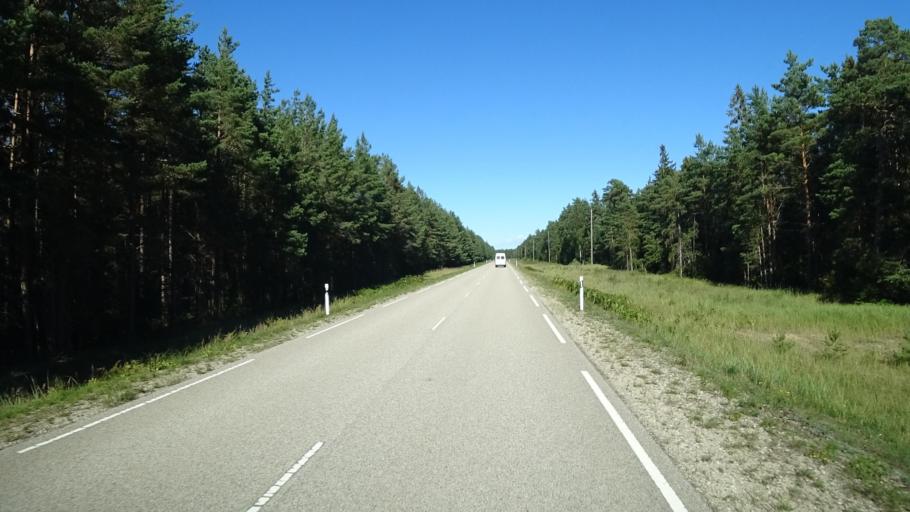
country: LV
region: Dundaga
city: Dundaga
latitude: 57.7305
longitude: 22.5093
